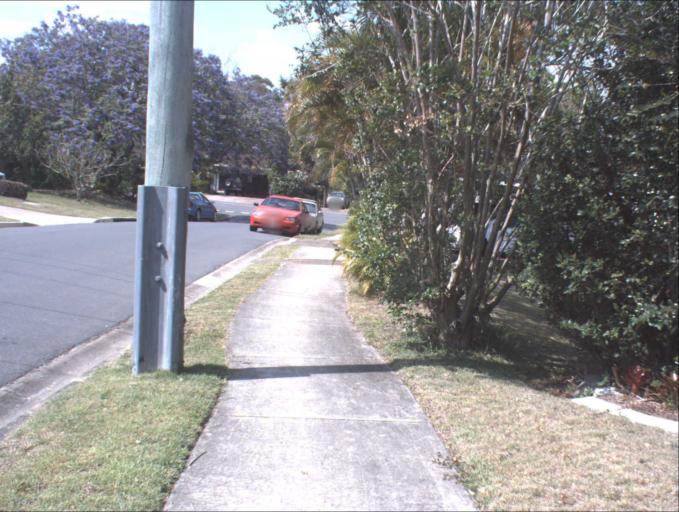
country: AU
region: Queensland
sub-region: Logan
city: Springwood
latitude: -27.6132
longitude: 153.1306
